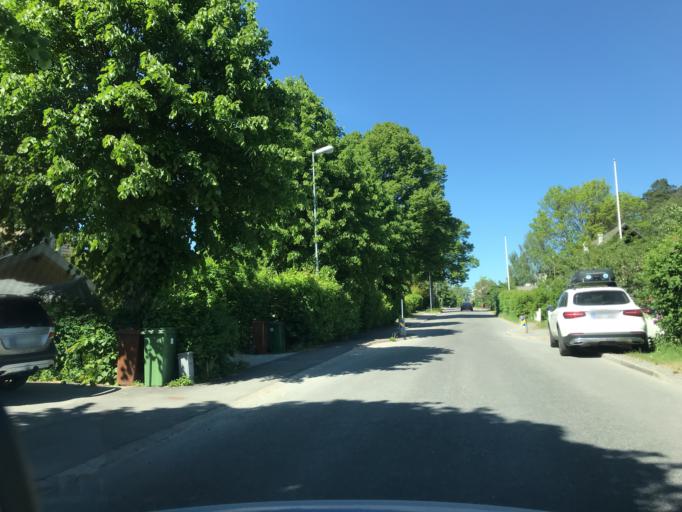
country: SE
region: Stockholm
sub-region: Sollentuna Kommun
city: Sollentuna
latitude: 59.4123
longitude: 17.9732
